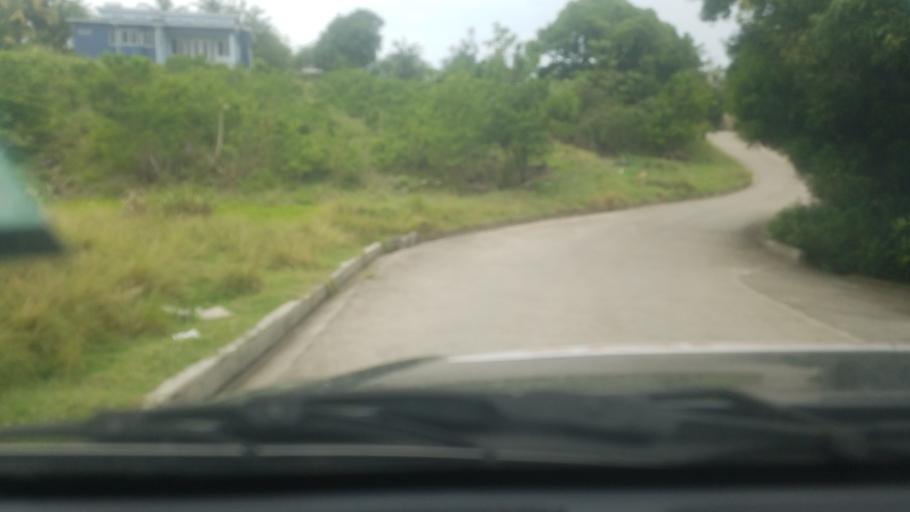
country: LC
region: Laborie Quarter
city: Laborie
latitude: 13.7499
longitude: -60.9802
